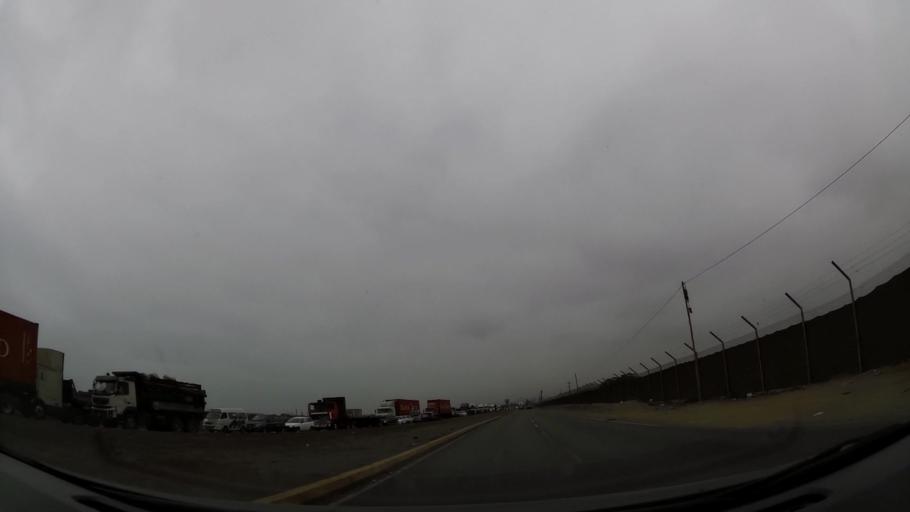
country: PE
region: Callao
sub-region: Callao
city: Callao
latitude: -12.0182
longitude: -77.1298
